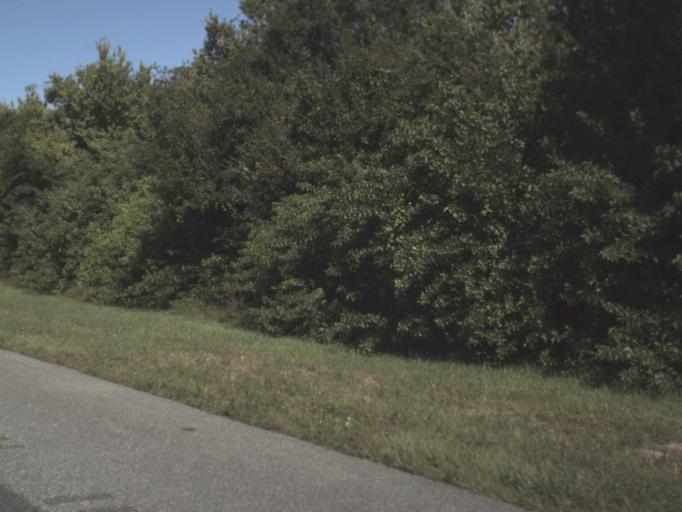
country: US
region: Florida
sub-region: Osceola County
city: Saint Cloud
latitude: 28.0785
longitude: -81.2553
